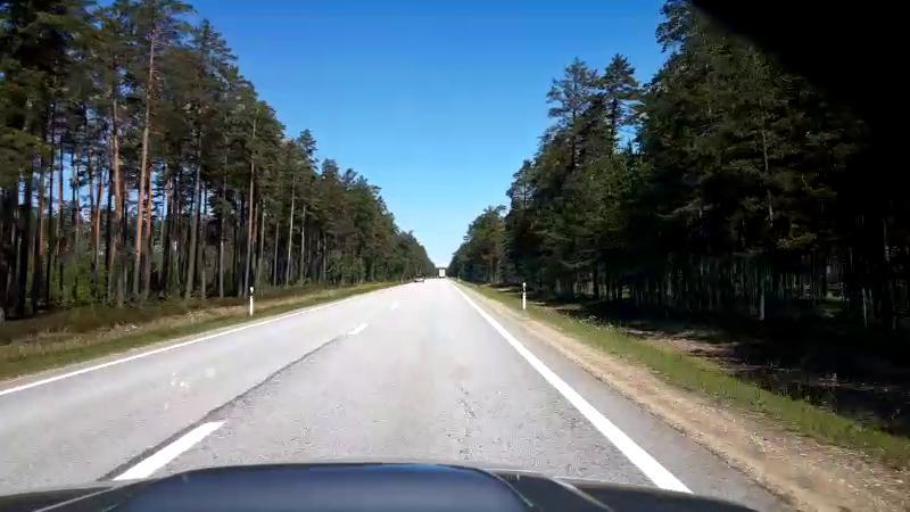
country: LV
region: Salacgrivas
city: Salacgriva
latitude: 57.5594
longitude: 24.4337
